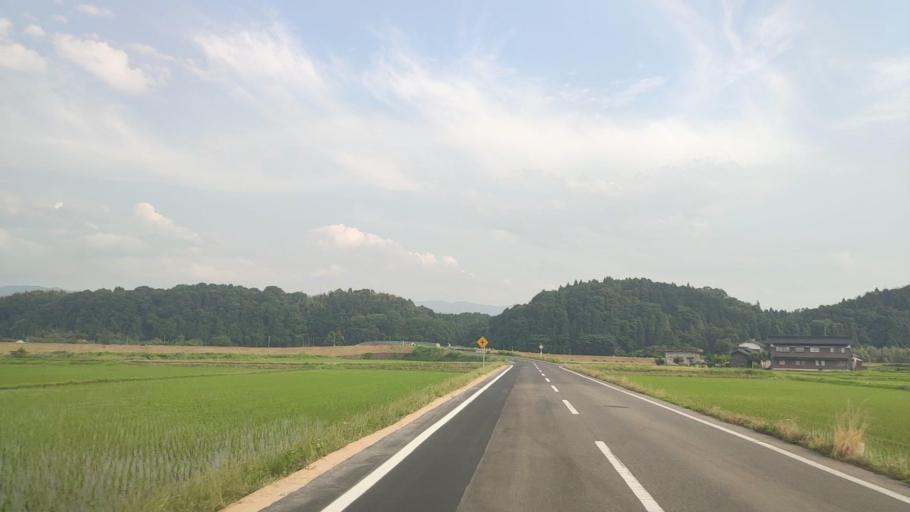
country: JP
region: Tottori
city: Kurayoshi
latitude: 35.4198
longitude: 133.7816
